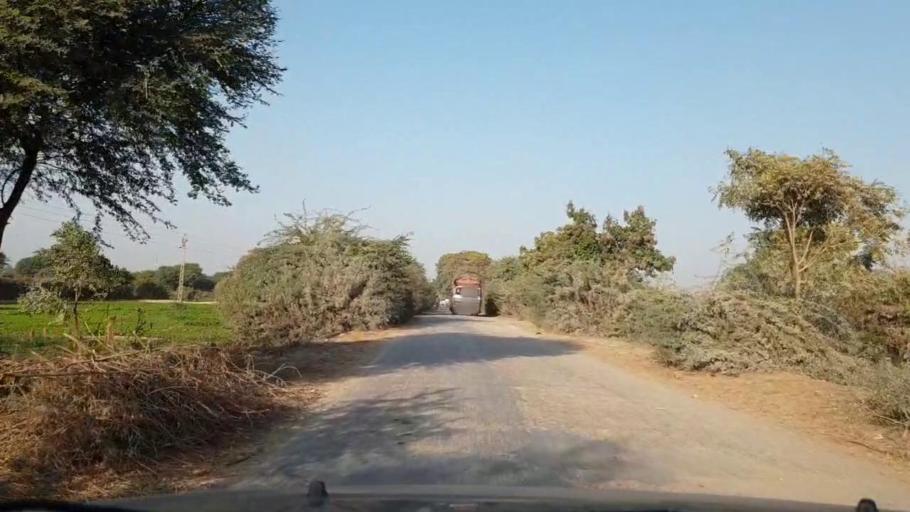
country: PK
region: Sindh
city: Chambar
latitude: 25.2821
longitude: 68.8096
